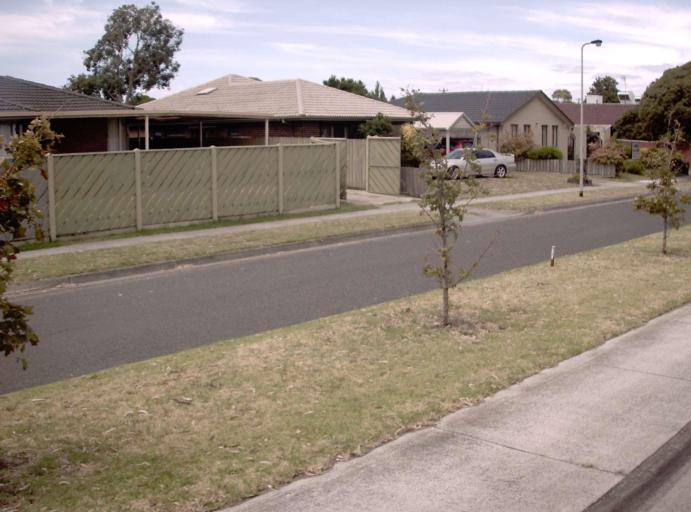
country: AU
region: Victoria
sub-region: Greater Dandenong
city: Keysborough
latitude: -37.9933
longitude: 145.1661
